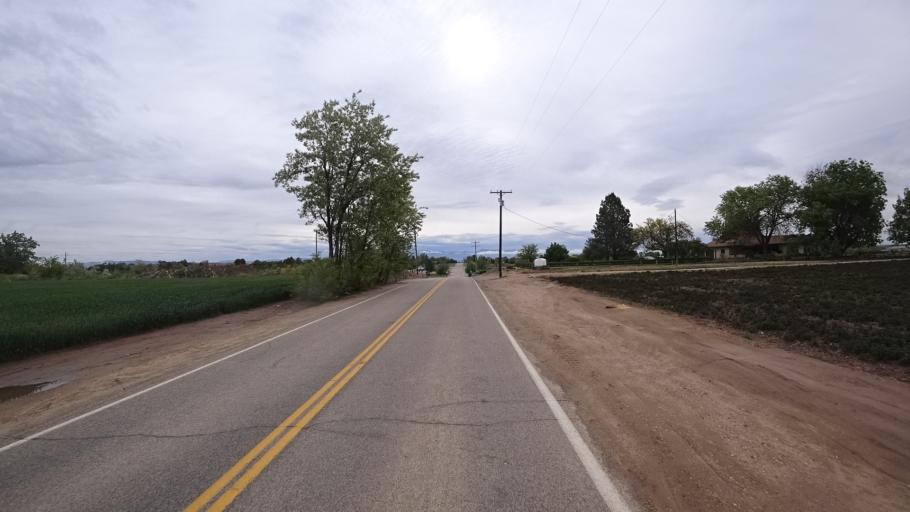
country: US
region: Idaho
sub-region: Ada County
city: Star
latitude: 43.7212
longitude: -116.4718
